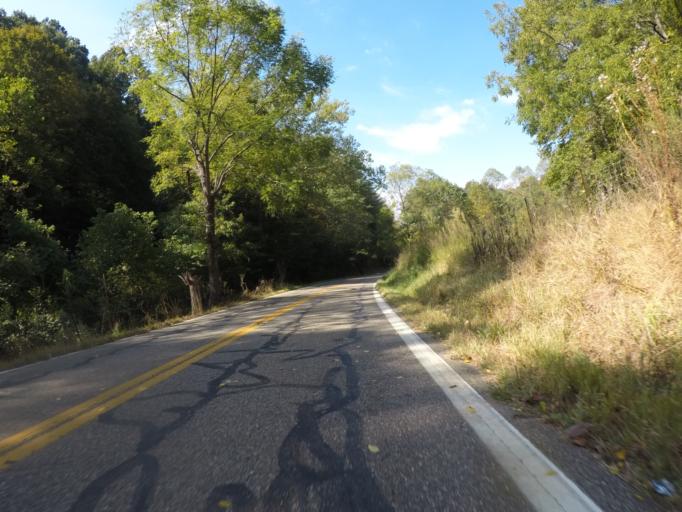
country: US
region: West Virginia
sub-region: Cabell County
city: Lesage
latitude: 38.6442
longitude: -82.4262
